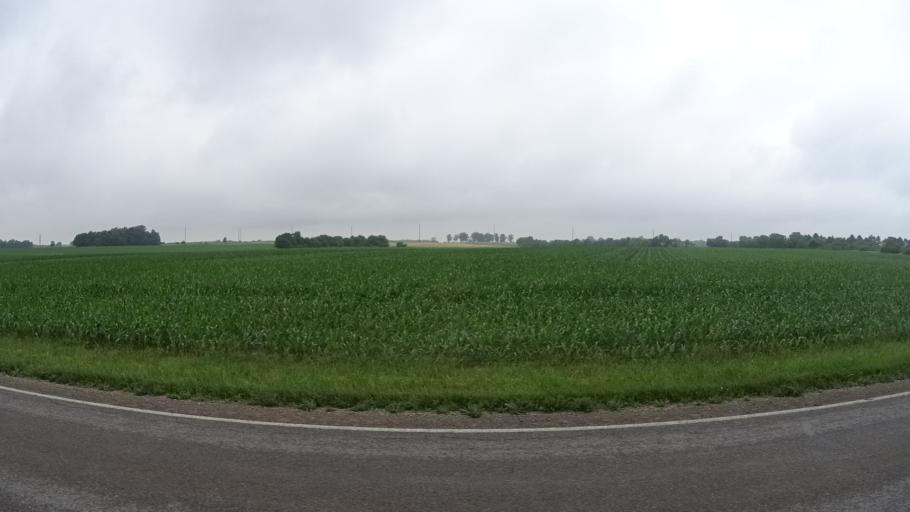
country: US
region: Ohio
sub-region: Huron County
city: Bellevue
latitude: 41.3479
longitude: -82.7585
